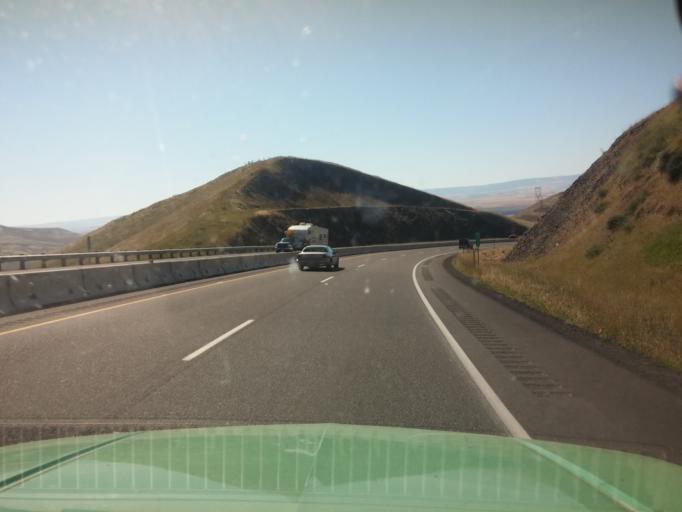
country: US
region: Idaho
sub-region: Nez Perce County
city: Lewiston
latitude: 46.4605
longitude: -116.9603
